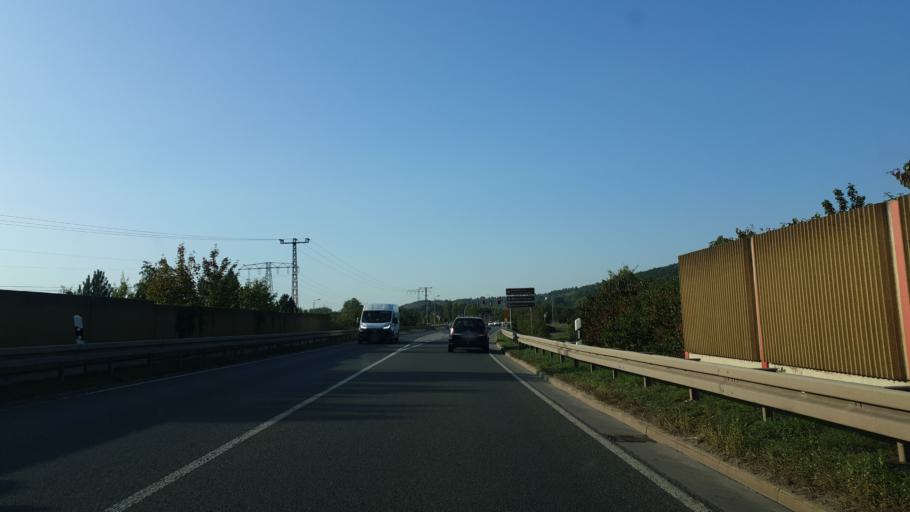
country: DE
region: Thuringia
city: Bad Kostritz
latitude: 50.9301
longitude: 12.0258
